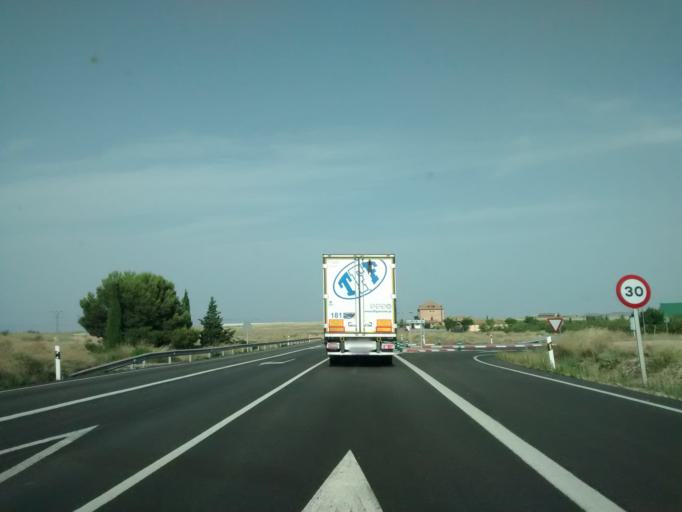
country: ES
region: Aragon
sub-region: Provincia de Zaragoza
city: Albeta
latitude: 41.8310
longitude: -1.5044
